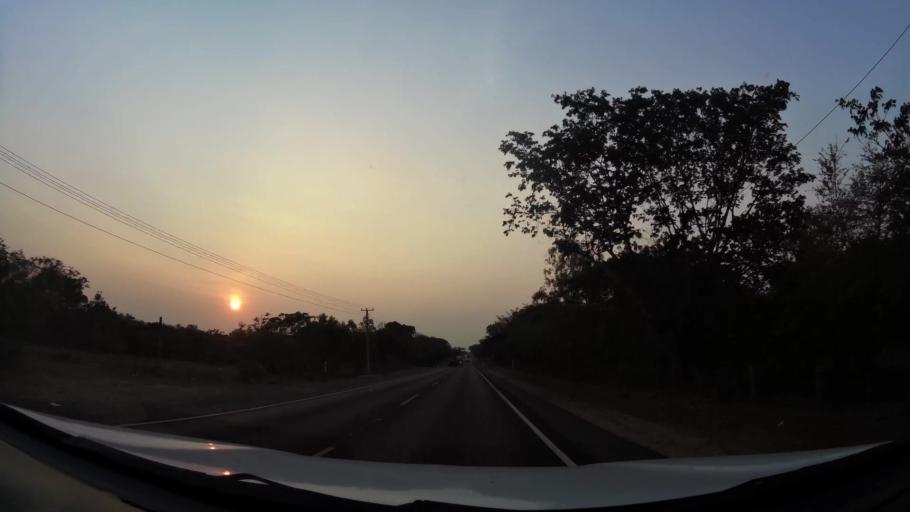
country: NI
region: Leon
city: Leon
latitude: 12.3447
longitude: -86.8212
